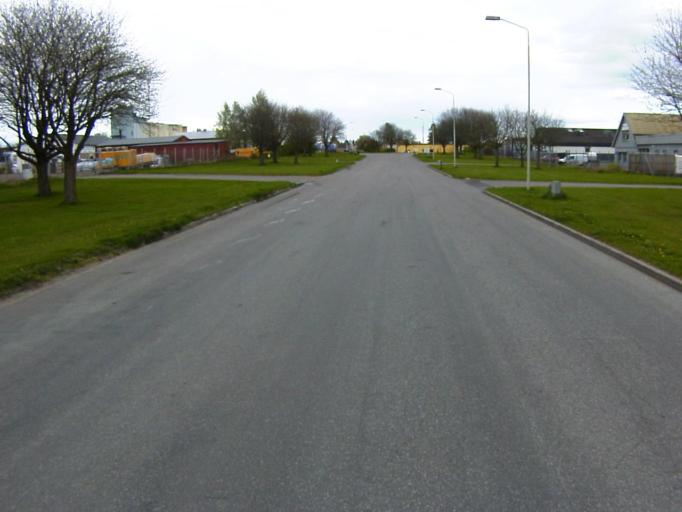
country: SE
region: Skane
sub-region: Kristianstads Kommun
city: Kristianstad
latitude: 56.0586
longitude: 14.1735
